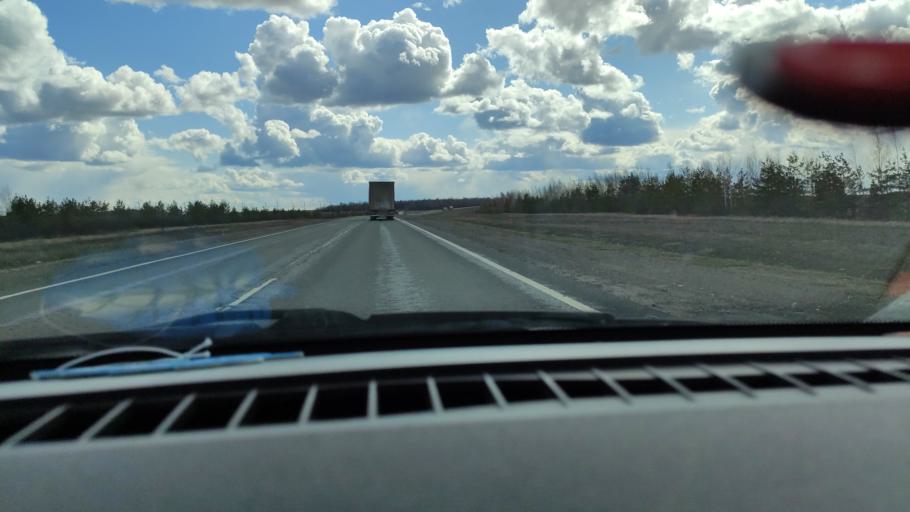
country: RU
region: Samara
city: Syzran'
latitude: 52.8756
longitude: 48.2894
